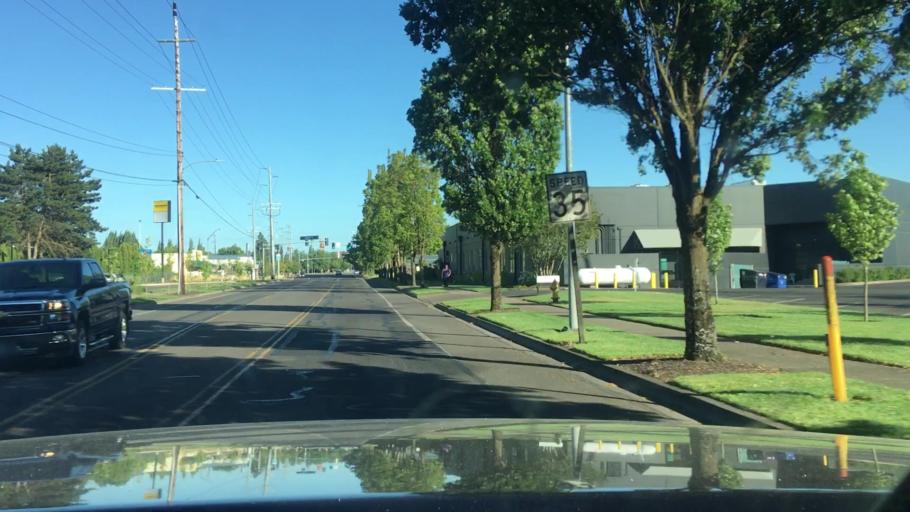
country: US
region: Oregon
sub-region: Lane County
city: Springfield
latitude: 44.0883
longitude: -123.0455
